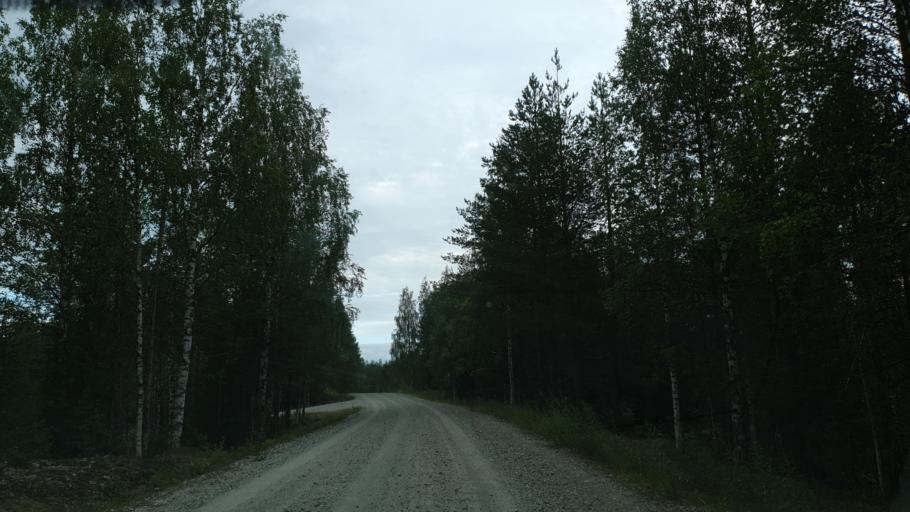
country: FI
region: Kainuu
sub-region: Kehys-Kainuu
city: Kuhmo
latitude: 64.4523
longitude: 29.5684
